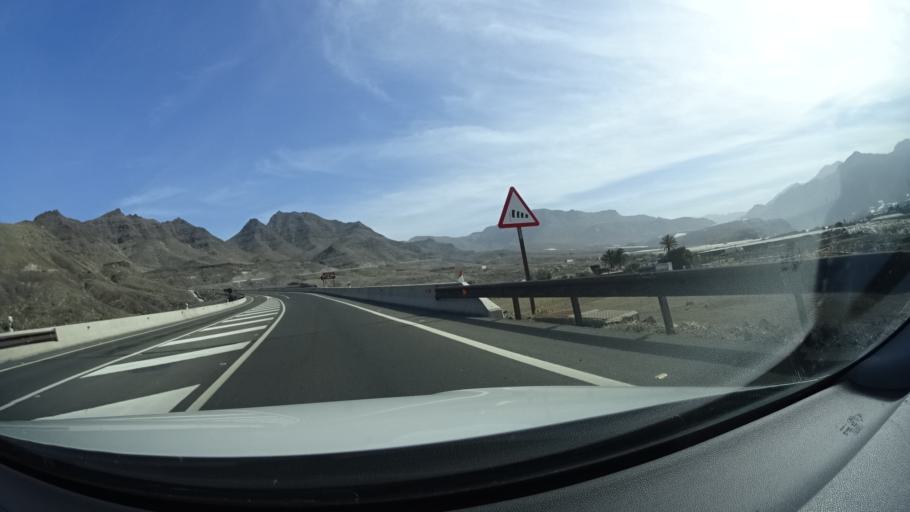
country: ES
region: Canary Islands
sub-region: Provincia de Las Palmas
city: San Nicolas
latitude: 28.0012
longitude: -15.8099
